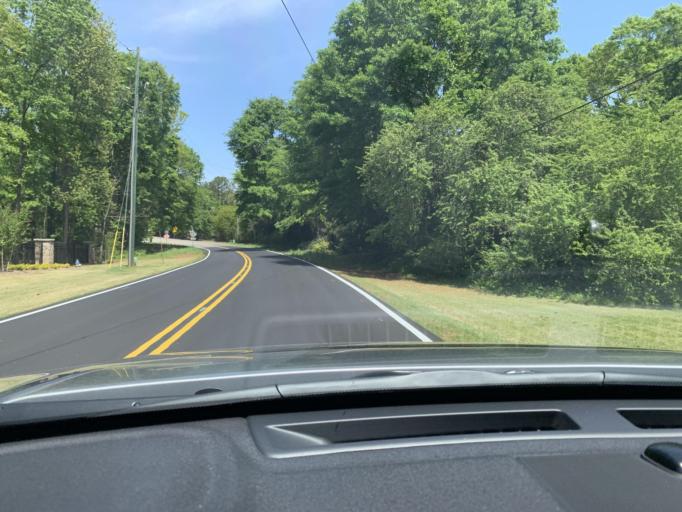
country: US
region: Georgia
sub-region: Oconee County
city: Bogart
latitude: 33.9076
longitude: -83.4749
